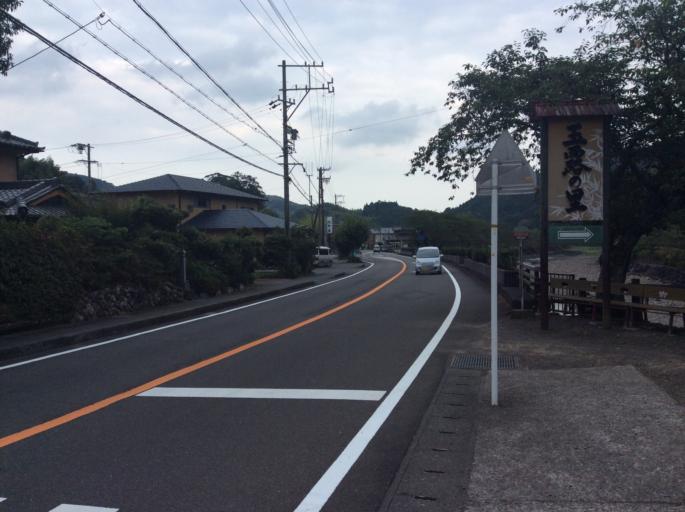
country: JP
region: Shizuoka
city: Fujieda
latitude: 34.9516
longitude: 138.2504
